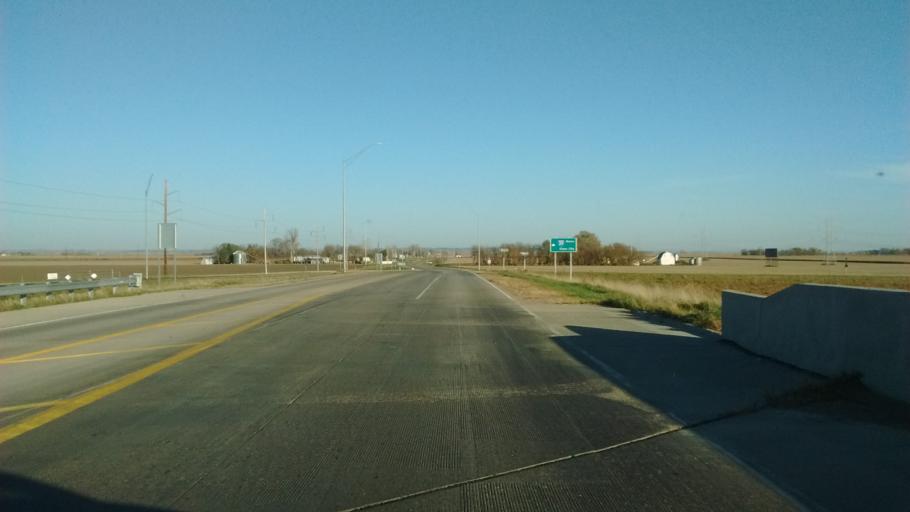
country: US
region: Iowa
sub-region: Woodbury County
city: Sergeant Bluff
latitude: 42.3299
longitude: -96.3179
